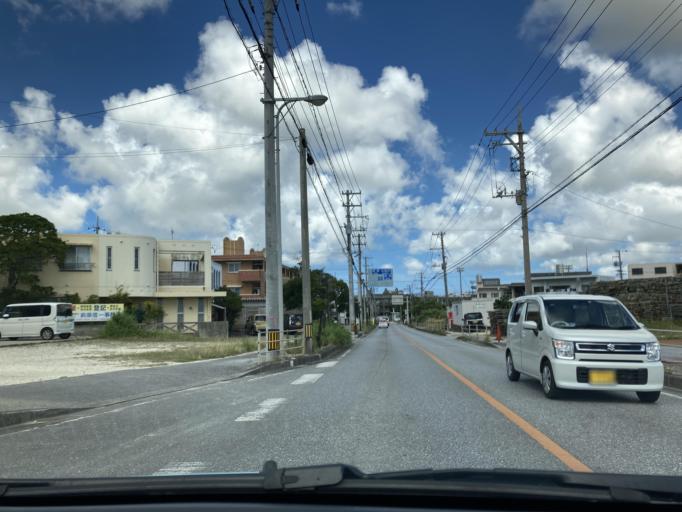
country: JP
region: Okinawa
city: Tomigusuku
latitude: 26.1487
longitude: 127.7245
